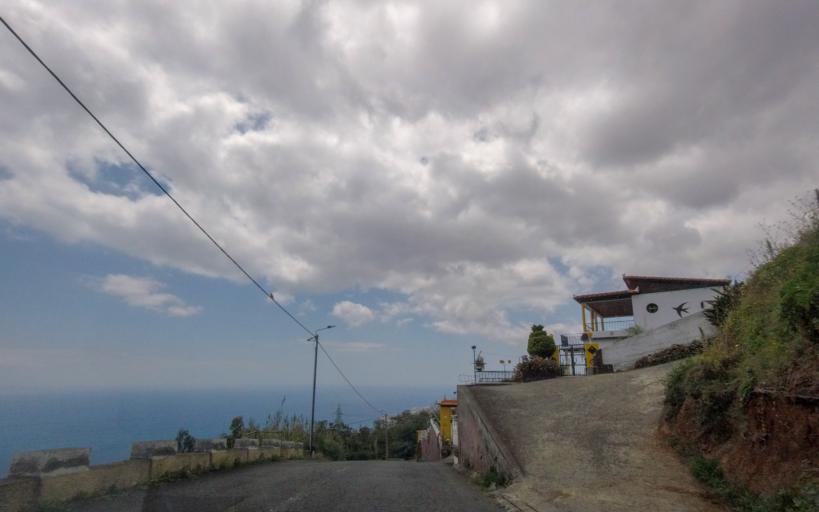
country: PT
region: Madeira
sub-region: Funchal
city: Nossa Senhora do Monte
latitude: 32.6648
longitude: -16.8818
